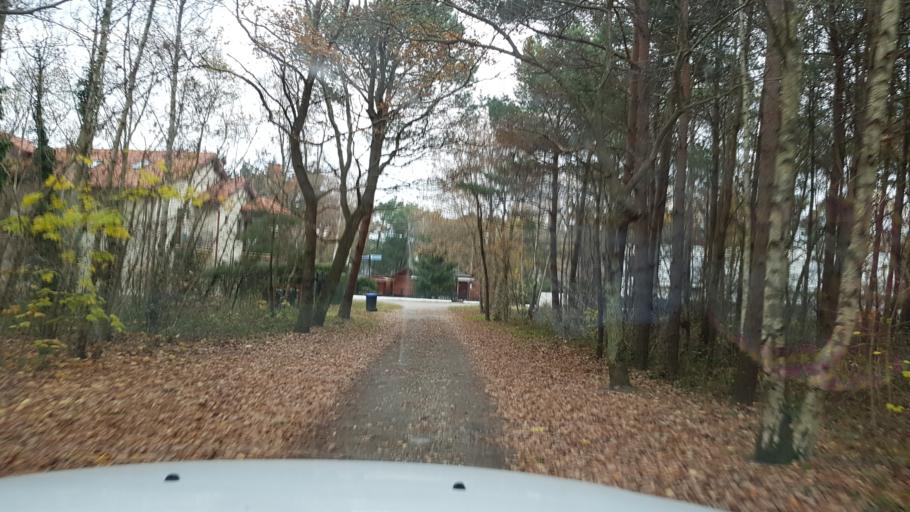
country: PL
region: West Pomeranian Voivodeship
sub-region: Powiat gryficki
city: Pobierowo
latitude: 54.0592
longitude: 14.9381
